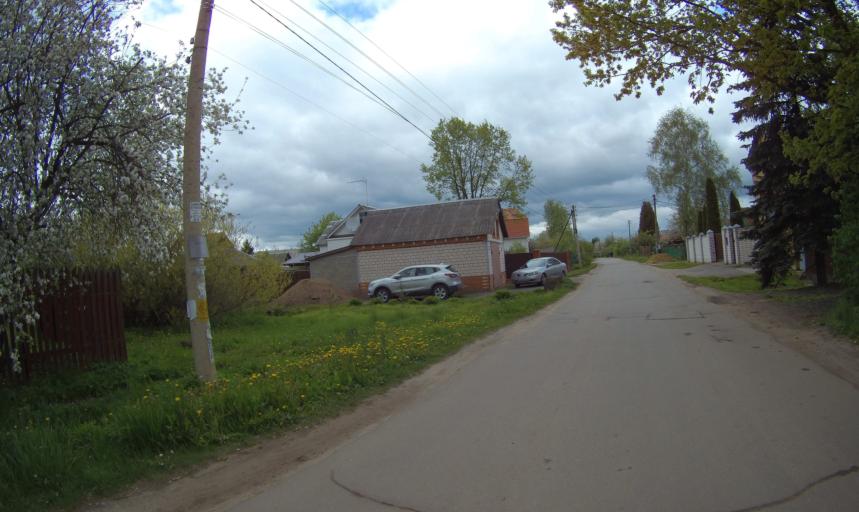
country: RU
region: Moskovskaya
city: Rechitsy
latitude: 55.5809
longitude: 38.5050
